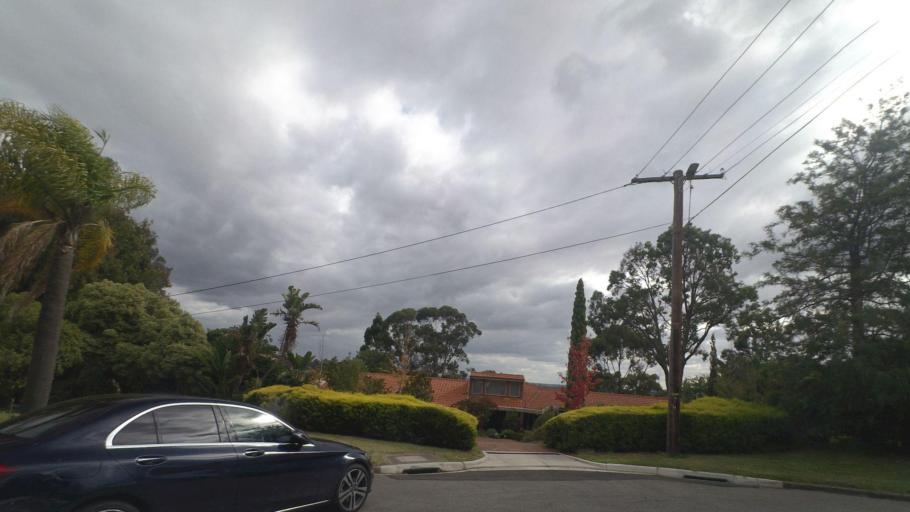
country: AU
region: Victoria
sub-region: Nillumbik
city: Eltham
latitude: -37.7580
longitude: 145.1497
